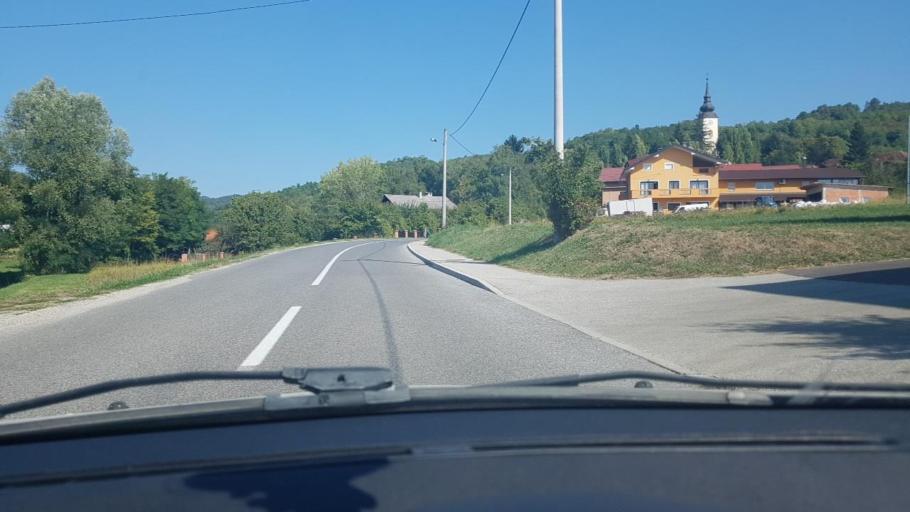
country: HR
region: Krapinsko-Zagorska
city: Marija Bistrica
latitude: 45.9349
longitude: 16.1673
